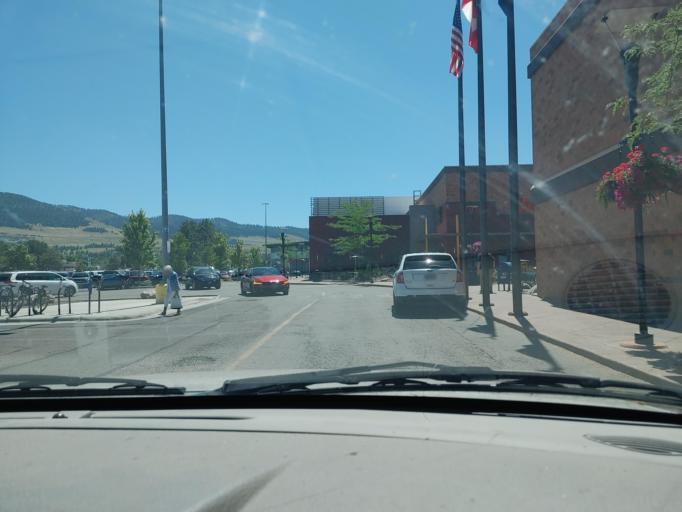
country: US
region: Montana
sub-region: Missoula County
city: Orchard Homes
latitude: 46.8464
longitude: -114.0263
